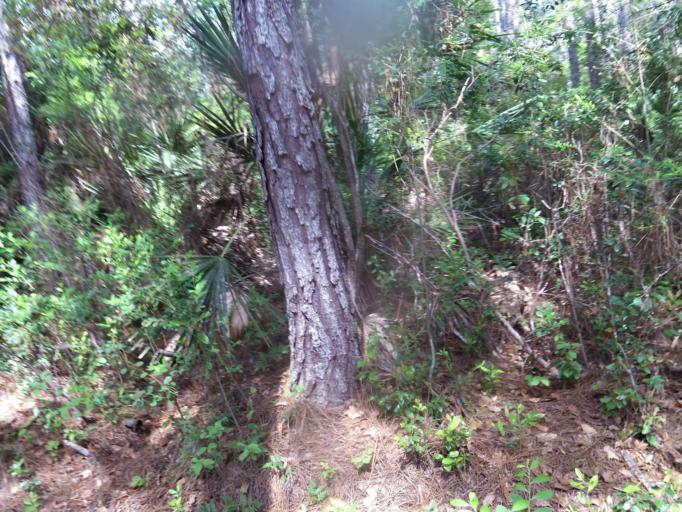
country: US
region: Florida
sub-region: Nassau County
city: Yulee
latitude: 30.4877
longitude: -81.4973
